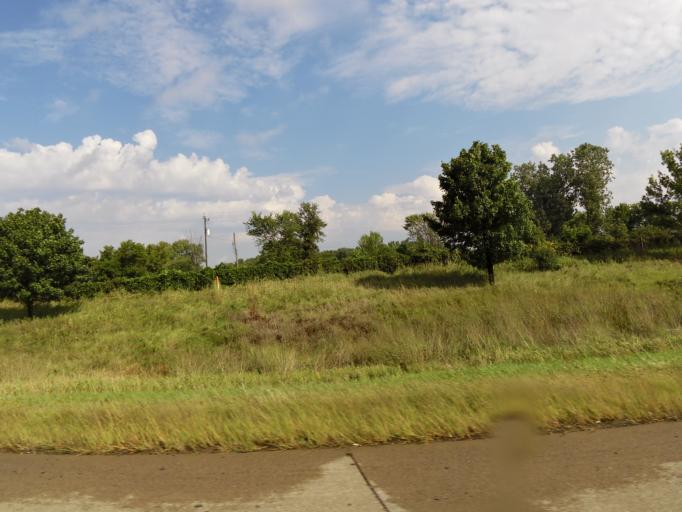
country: US
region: Minnesota
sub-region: Washington County
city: Lake Elmo
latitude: 44.9489
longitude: -92.8759
